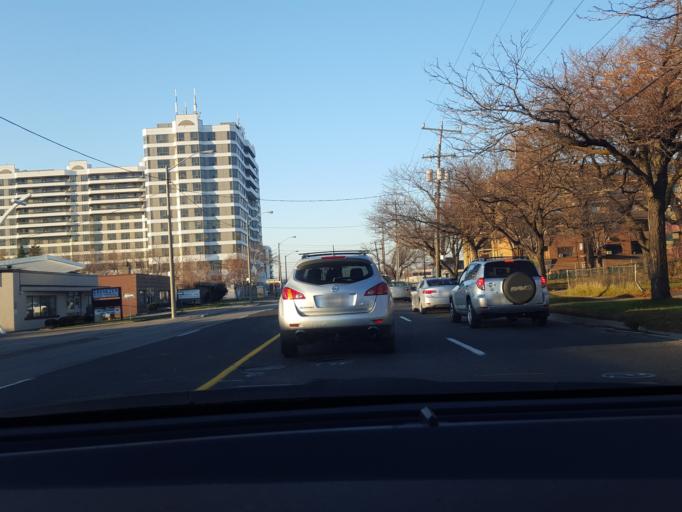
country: CA
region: Ontario
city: Scarborough
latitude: 43.7456
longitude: -79.2840
